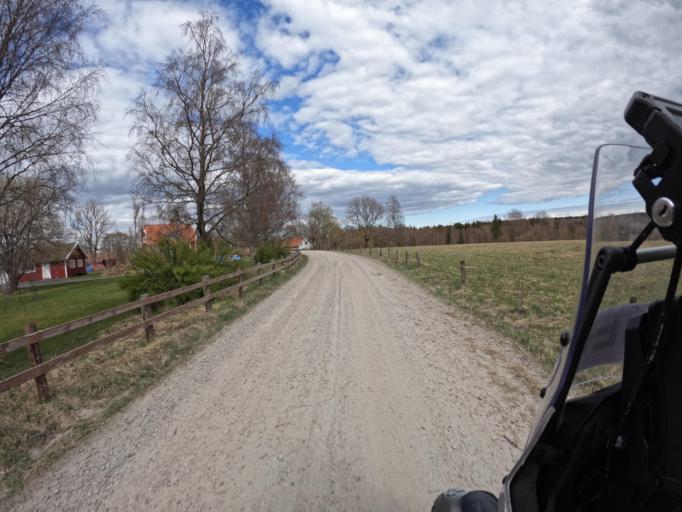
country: SE
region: Joenkoeping
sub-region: Mullsjo Kommun
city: Mullsjoe
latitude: 57.9014
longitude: 13.6526
